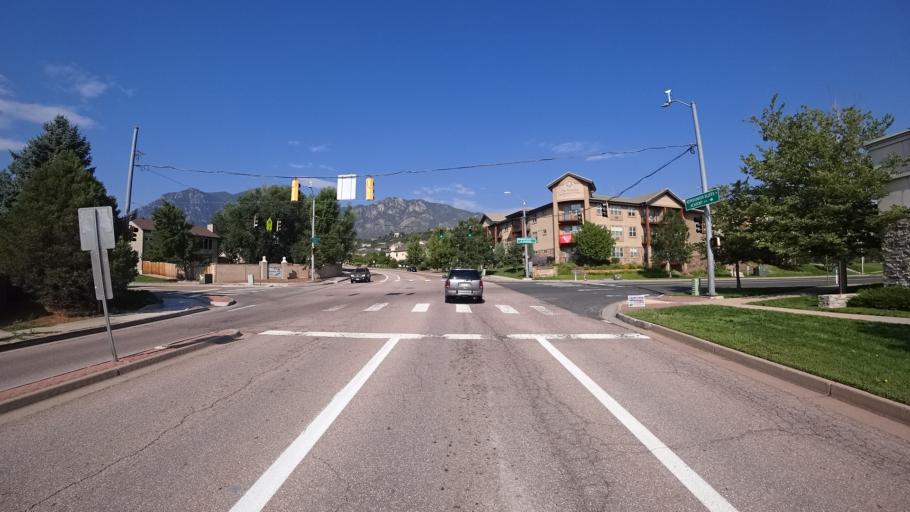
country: US
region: Colorado
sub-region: El Paso County
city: Stratmoor
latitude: 38.7659
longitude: -104.8161
